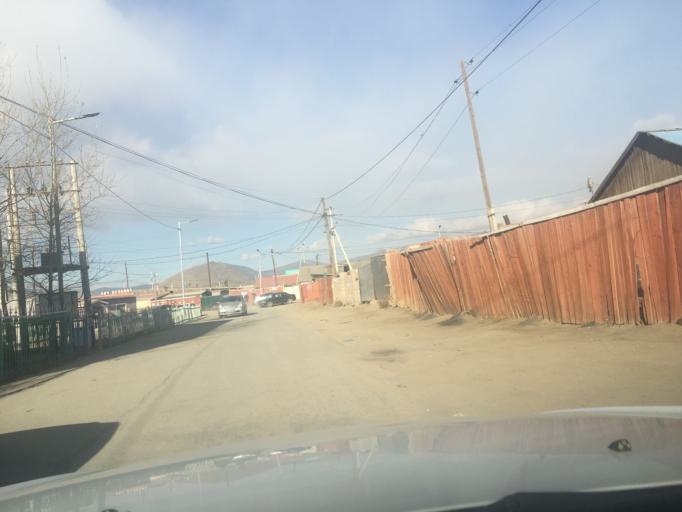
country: MN
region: Ulaanbaatar
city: Ulaanbaatar
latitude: 47.9457
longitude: 106.8253
